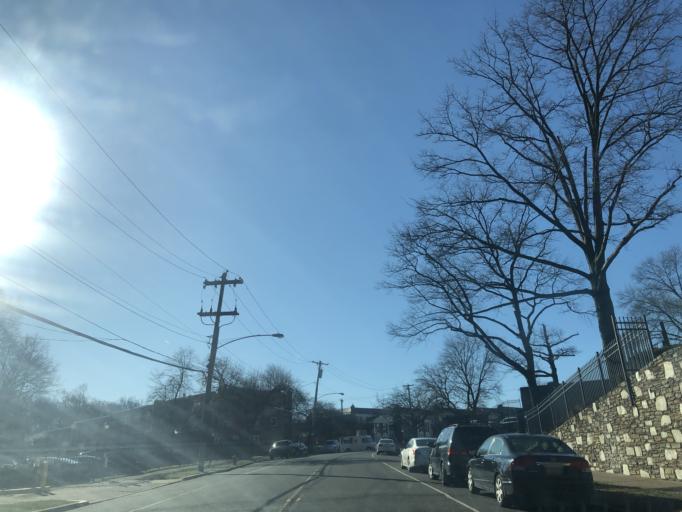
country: US
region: Pennsylvania
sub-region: Montgomery County
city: Bala-Cynwyd
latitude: 40.0041
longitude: -75.2024
